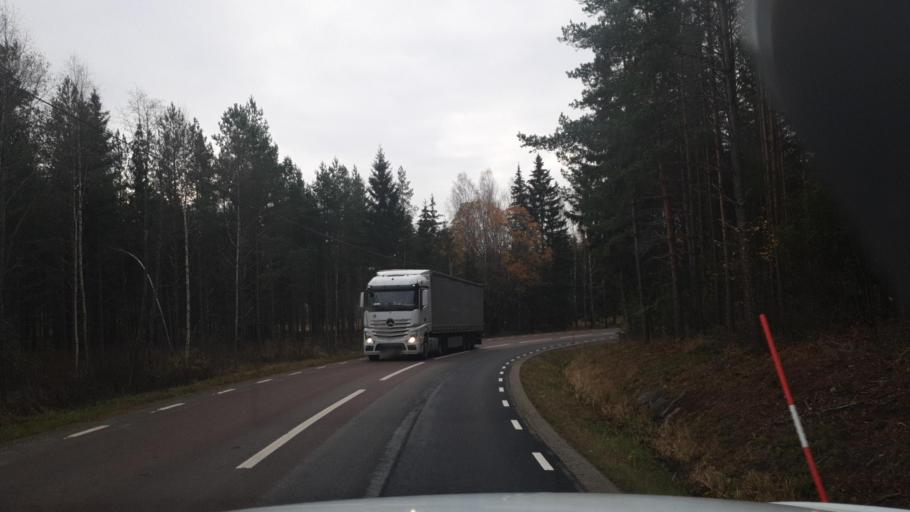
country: SE
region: Vaermland
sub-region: Sunne Kommun
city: Sunne
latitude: 59.6597
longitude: 12.9593
